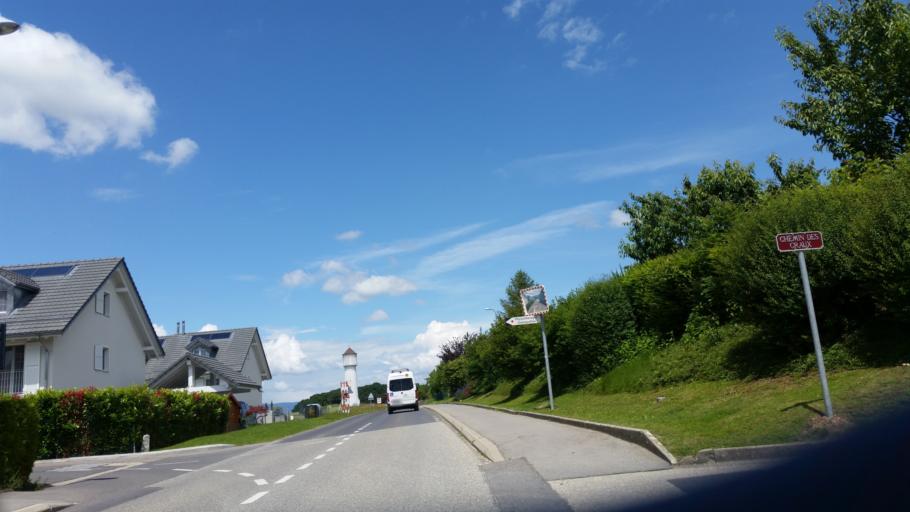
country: CH
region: Vaud
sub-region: Gros-de-Vaud District
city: Penthereaz
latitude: 46.6608
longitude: 6.6070
